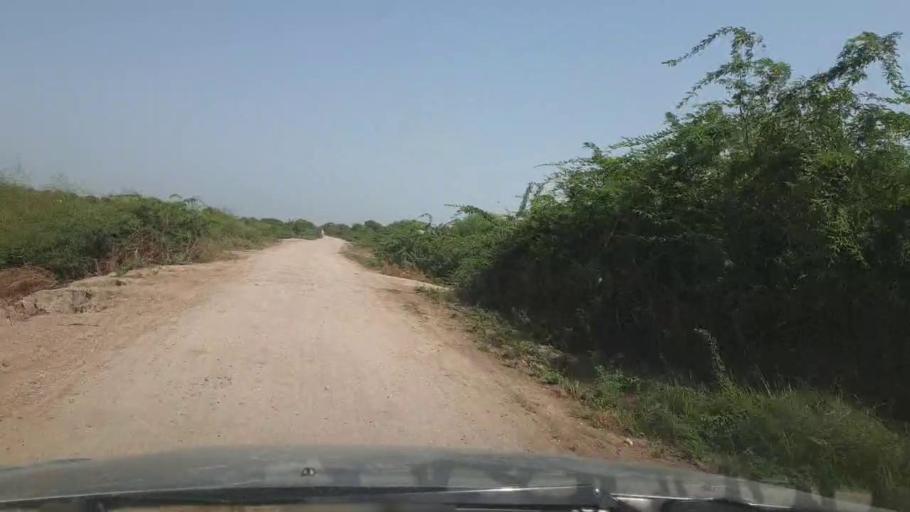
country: PK
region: Sindh
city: Tando Ghulam Ali
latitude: 25.1545
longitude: 68.8982
